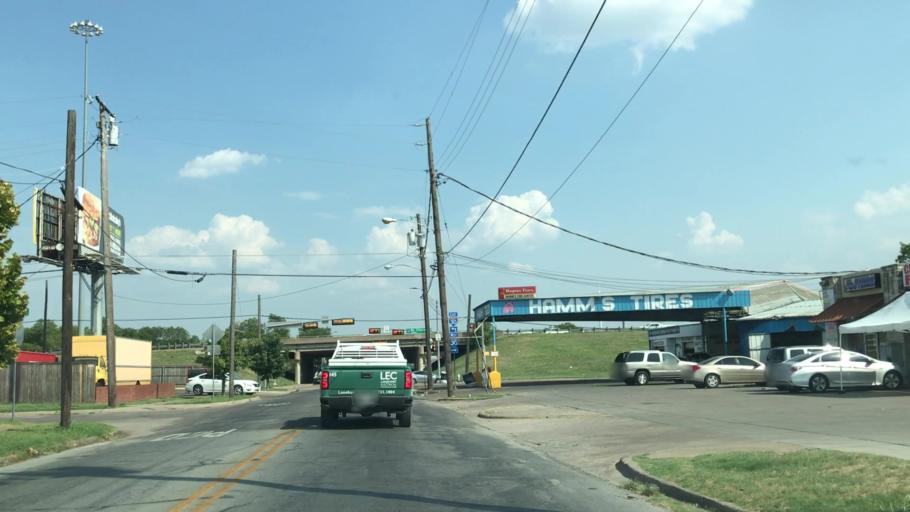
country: US
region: Texas
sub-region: Dallas County
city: Dallas
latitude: 32.7897
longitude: -96.7654
